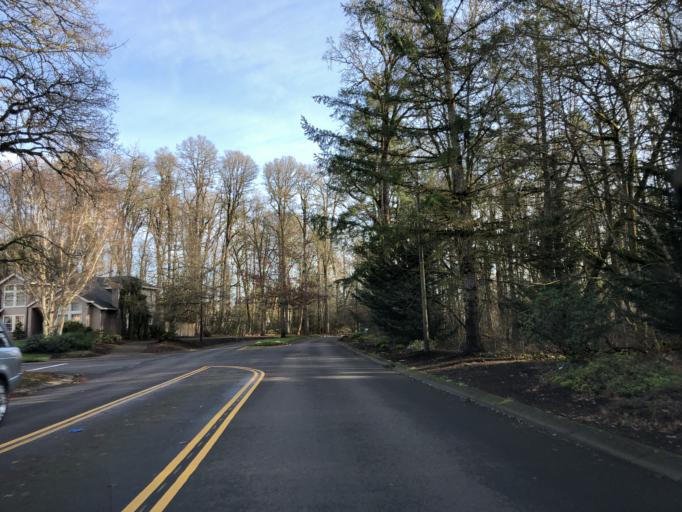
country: US
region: Oregon
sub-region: Washington County
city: Durham
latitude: 45.4229
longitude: -122.7340
